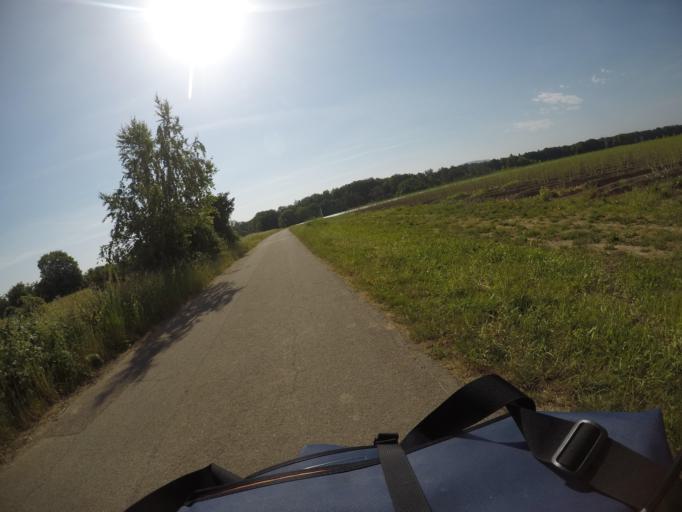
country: DE
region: Baden-Wuerttemberg
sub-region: Karlsruhe Region
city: Durmersheim
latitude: 48.9093
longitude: 8.2802
